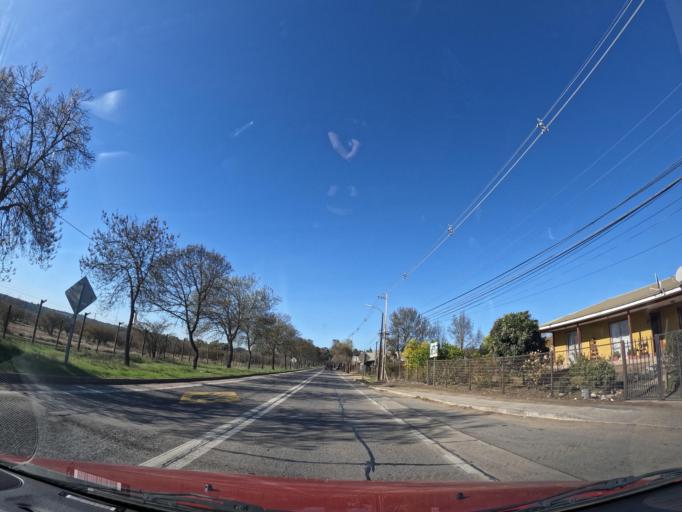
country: CL
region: Maule
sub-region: Provincia de Cauquenes
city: Cauquenes
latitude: -35.9579
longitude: -72.2978
